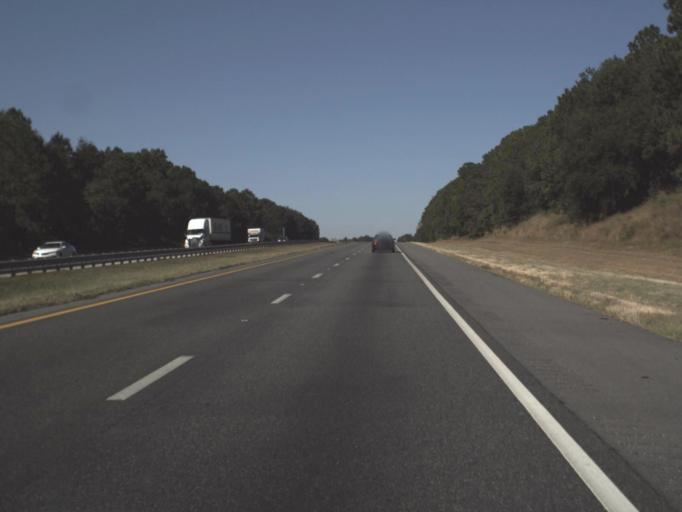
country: US
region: Florida
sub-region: Orange County
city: Oakland
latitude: 28.5563
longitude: -81.6698
